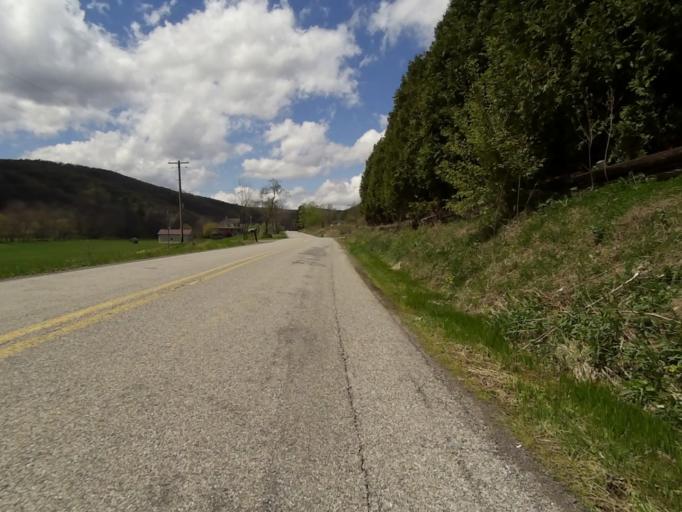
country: US
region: Pennsylvania
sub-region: Centre County
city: Milesburg
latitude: 40.9204
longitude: -77.8626
